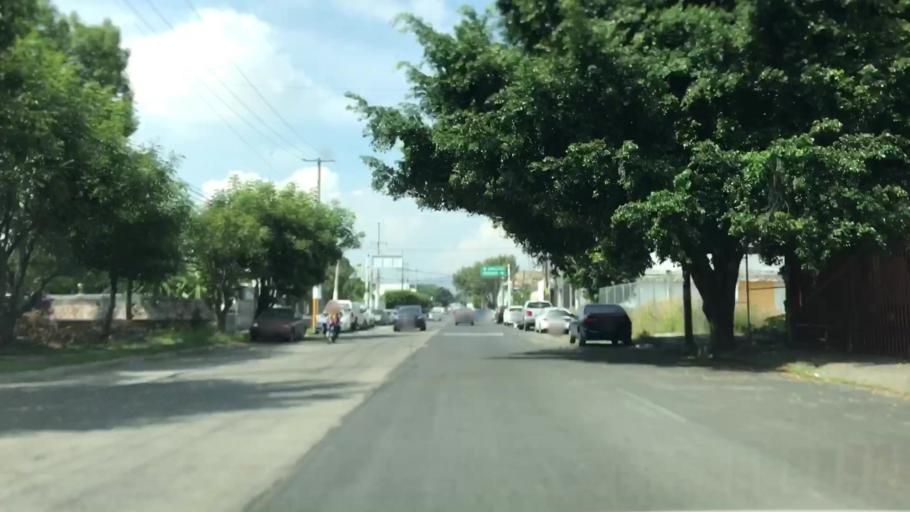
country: MX
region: Jalisco
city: Guadalajara
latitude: 20.6400
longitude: -103.4253
